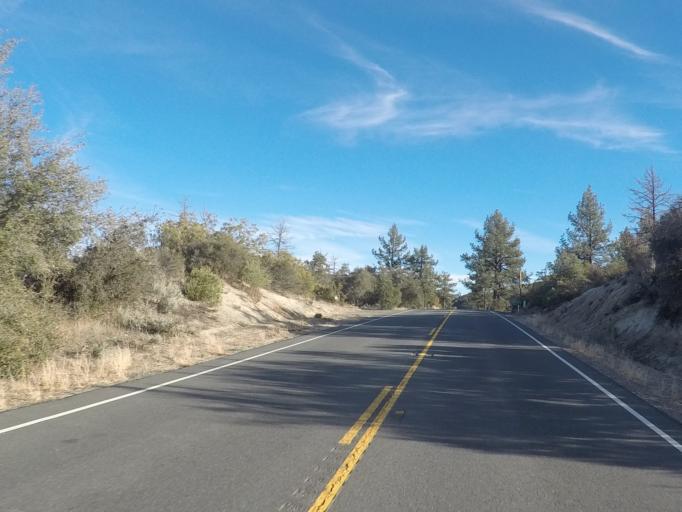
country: US
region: California
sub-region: Riverside County
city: Anza
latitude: 33.5787
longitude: -116.5982
